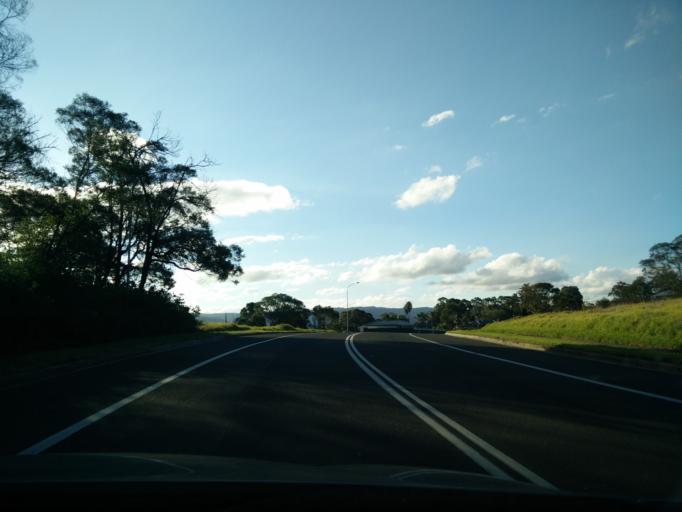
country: AU
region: New South Wales
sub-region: Wollongong
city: Berkeley
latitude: -34.4706
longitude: 150.8441
